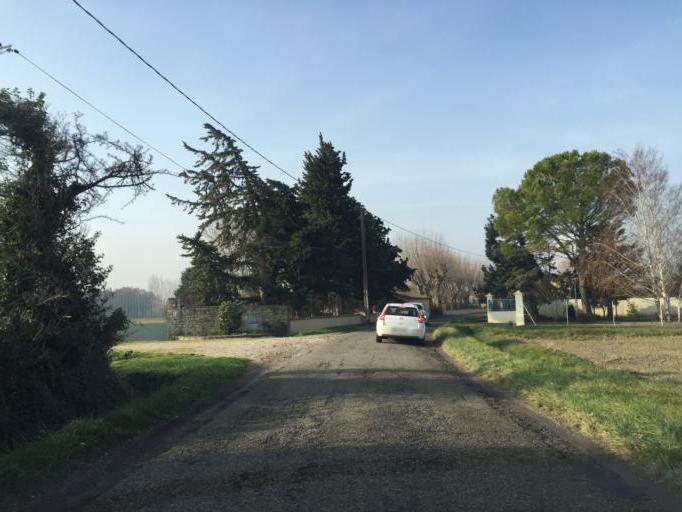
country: FR
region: Provence-Alpes-Cote d'Azur
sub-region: Departement du Vaucluse
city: Jonquieres
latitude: 44.1261
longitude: 4.8914
